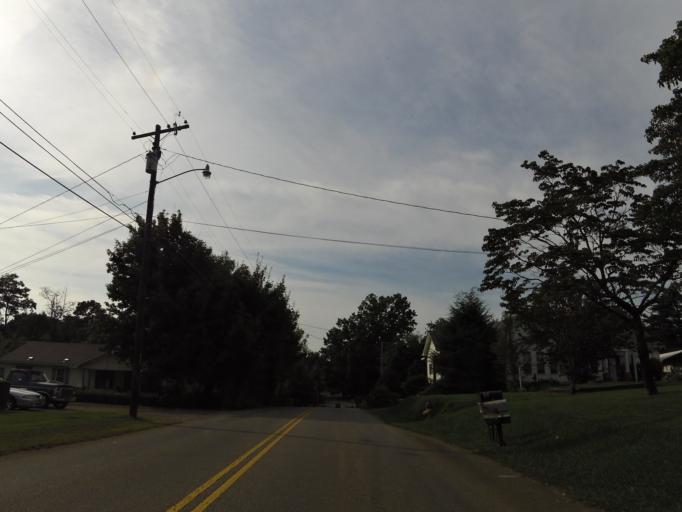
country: US
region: Tennessee
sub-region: Blount County
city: Maryville
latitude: 35.7635
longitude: -83.9523
